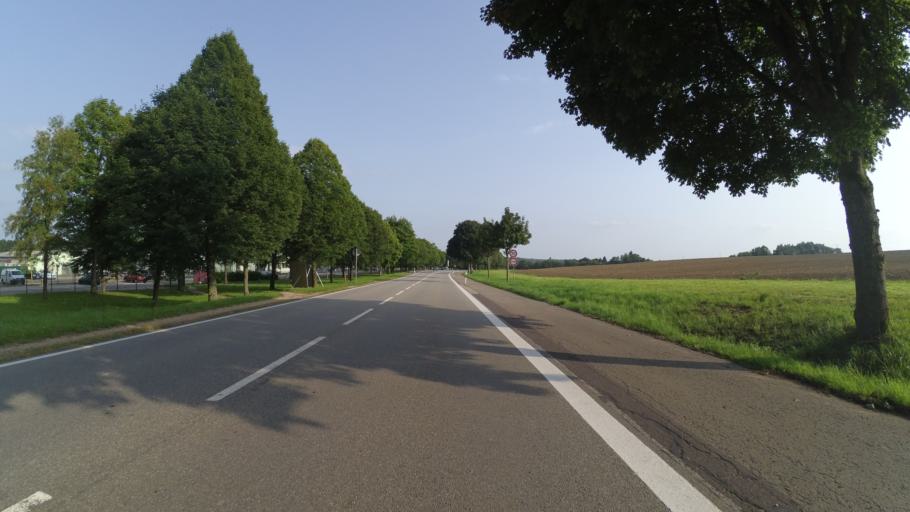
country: DE
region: Saarland
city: Weiskirchen
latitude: 49.5495
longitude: 6.8285
